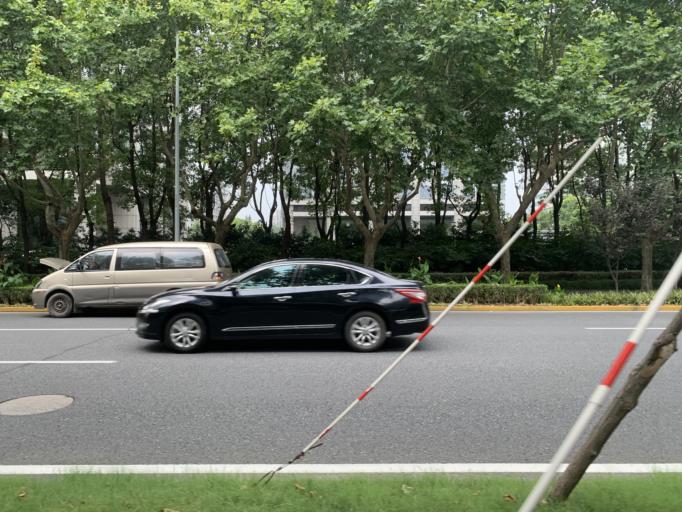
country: CN
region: Shanghai Shi
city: Huamu
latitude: 31.2218
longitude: 121.5464
